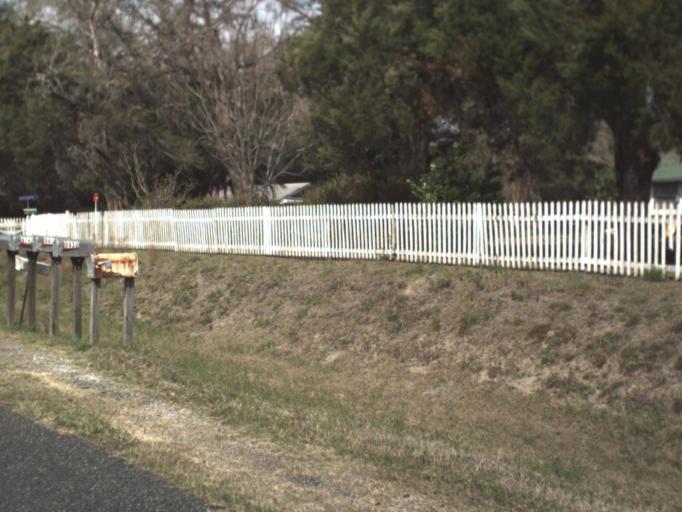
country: US
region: Florida
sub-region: Leon County
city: Tallahassee
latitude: 30.4225
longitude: -84.1103
